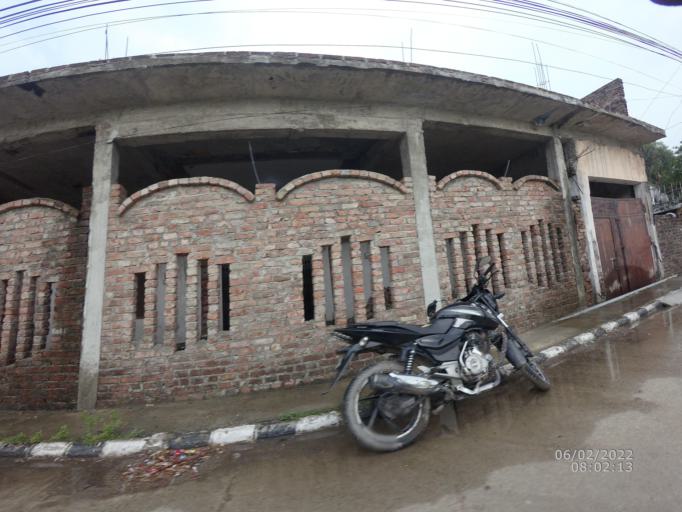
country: NP
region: Western Region
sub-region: Lumbini Zone
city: Bhairahawa
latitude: 27.4782
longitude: 83.4741
